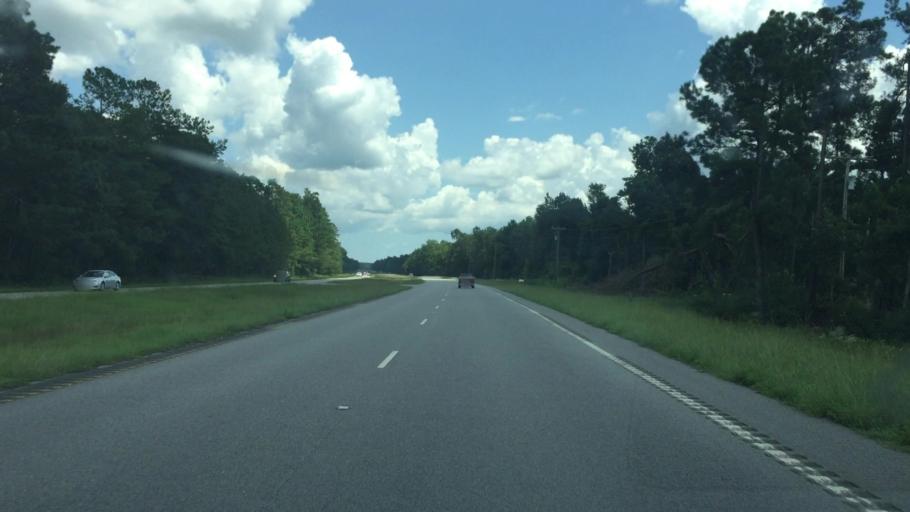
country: US
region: South Carolina
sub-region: Horry County
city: Loris
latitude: 34.0471
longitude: -78.8330
